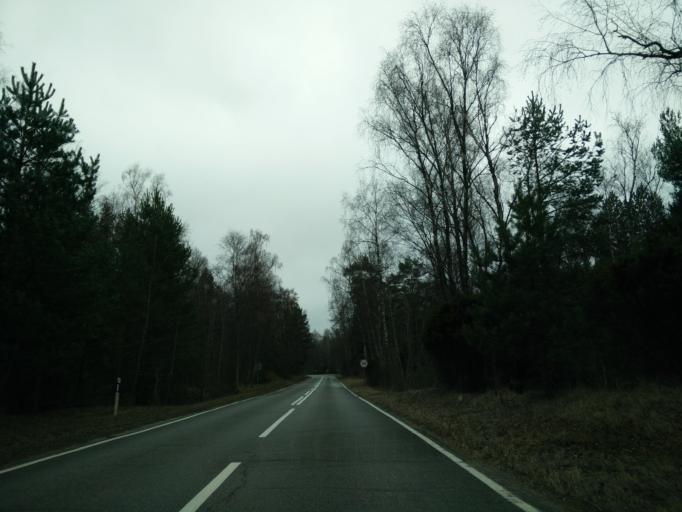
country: LT
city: Neringa
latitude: 55.4464
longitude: 21.0730
